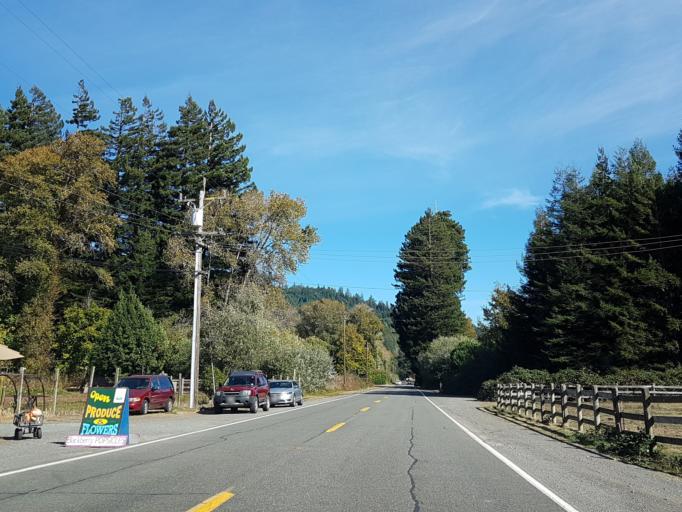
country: US
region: California
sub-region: Humboldt County
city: Rio Dell
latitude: 40.4461
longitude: -123.9962
